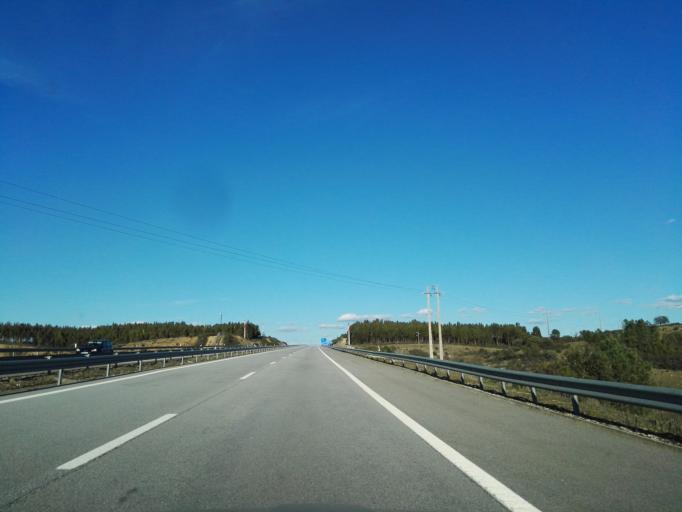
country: PT
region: Castelo Branco
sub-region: Castelo Branco
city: Castelo Branco
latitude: 39.8160
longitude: -7.5471
